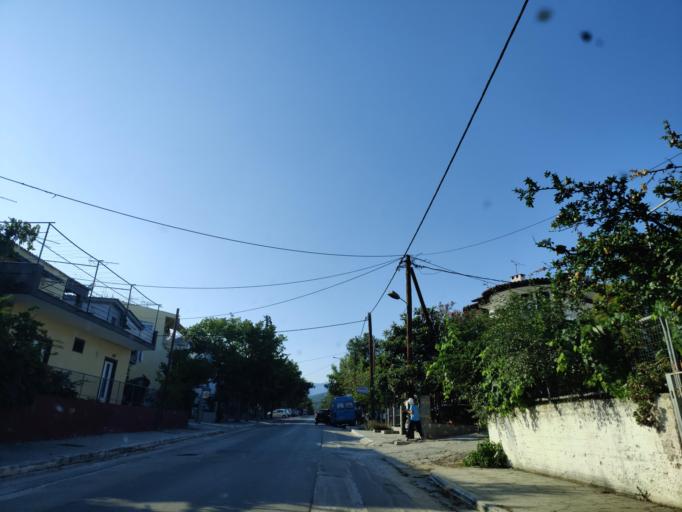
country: GR
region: East Macedonia and Thrace
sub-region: Nomos Kavalas
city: Limenaria
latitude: 40.6125
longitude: 24.6062
